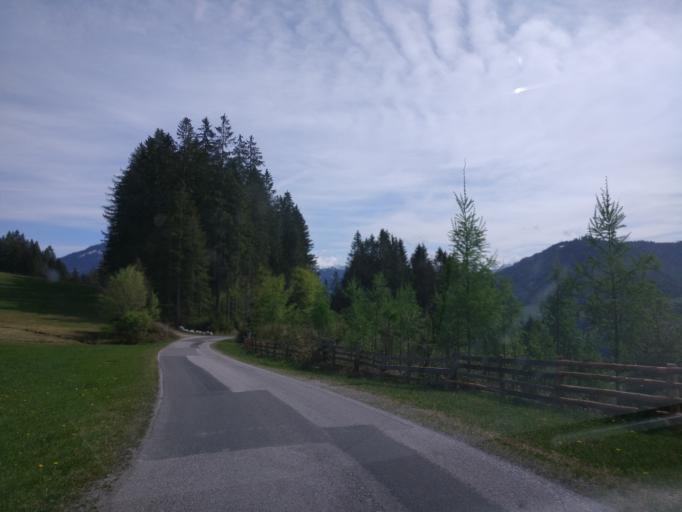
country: AT
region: Salzburg
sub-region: Politischer Bezirk Sankt Johann im Pongau
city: Pfarrwerfen
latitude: 47.4761
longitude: 13.2055
